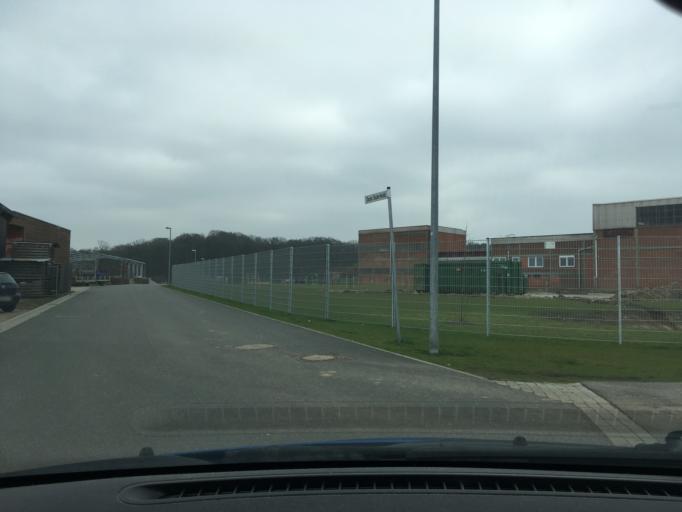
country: DE
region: Lower Saxony
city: Kirchgellersen
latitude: 53.2259
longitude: 10.2853
